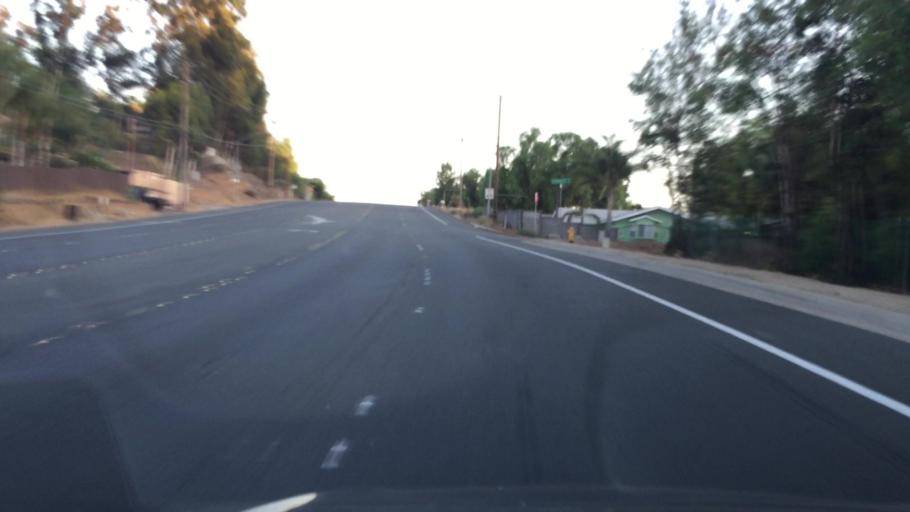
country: US
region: California
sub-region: San Diego County
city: Bostonia
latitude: 32.7787
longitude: -116.9280
